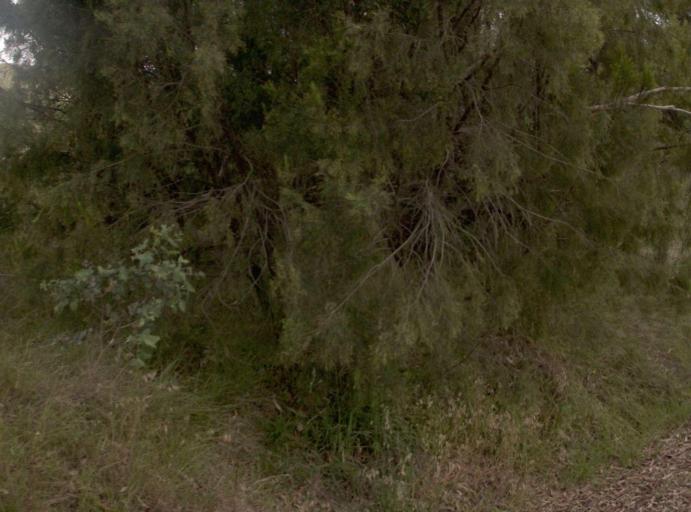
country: AU
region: Victoria
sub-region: East Gippsland
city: Bairnsdale
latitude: -37.7268
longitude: 147.5899
